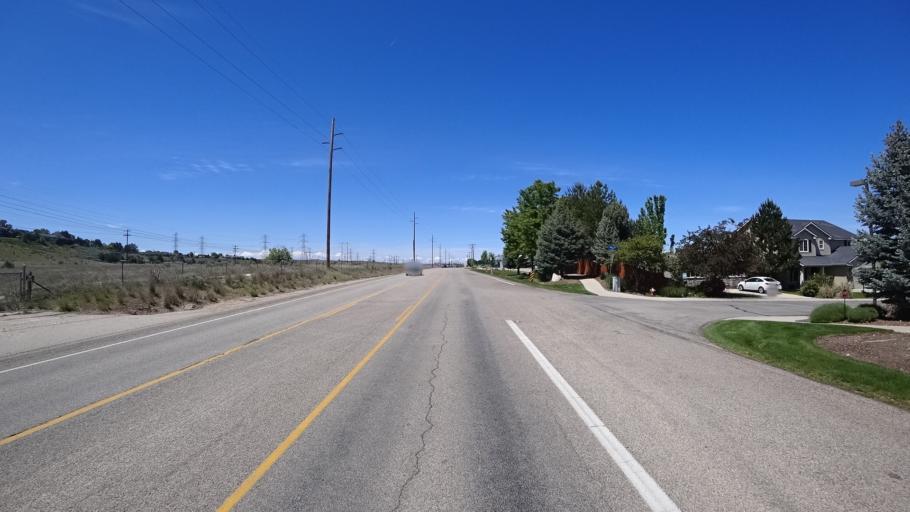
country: US
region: Idaho
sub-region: Ada County
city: Boise
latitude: 43.5600
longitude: -116.1410
